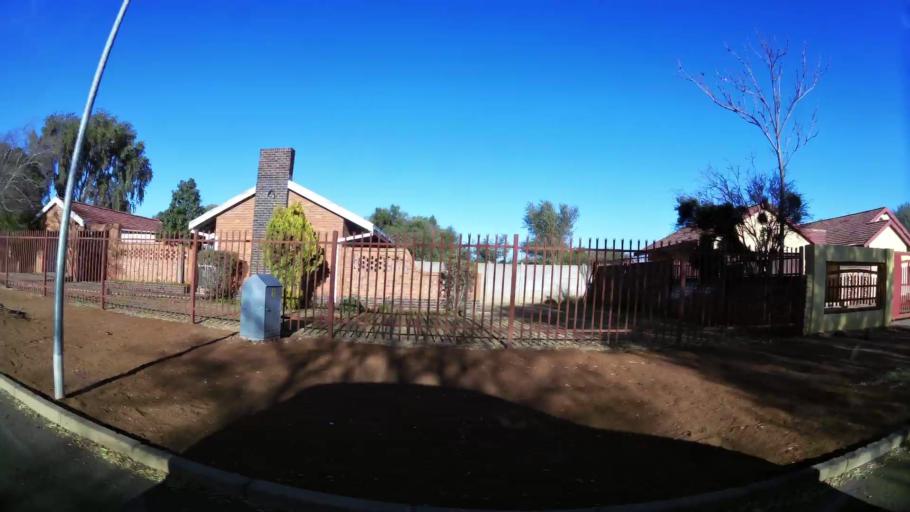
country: ZA
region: Northern Cape
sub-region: Frances Baard District Municipality
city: Kimberley
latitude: -28.7550
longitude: 24.7245
